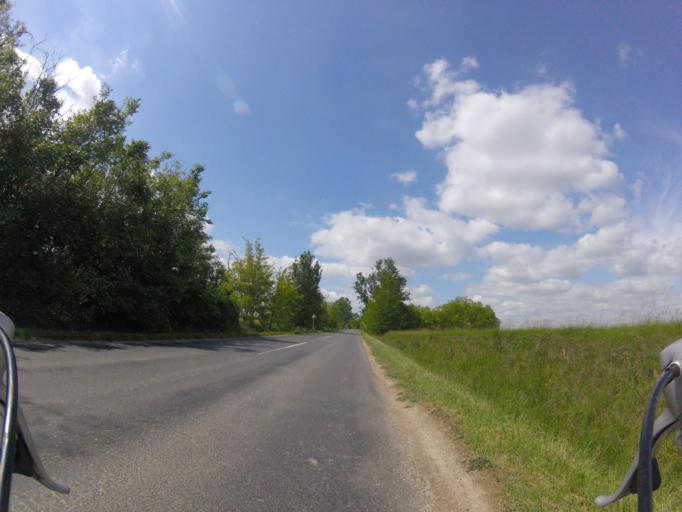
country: HU
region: Fejer
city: Soponya
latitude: 47.0300
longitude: 18.4427
